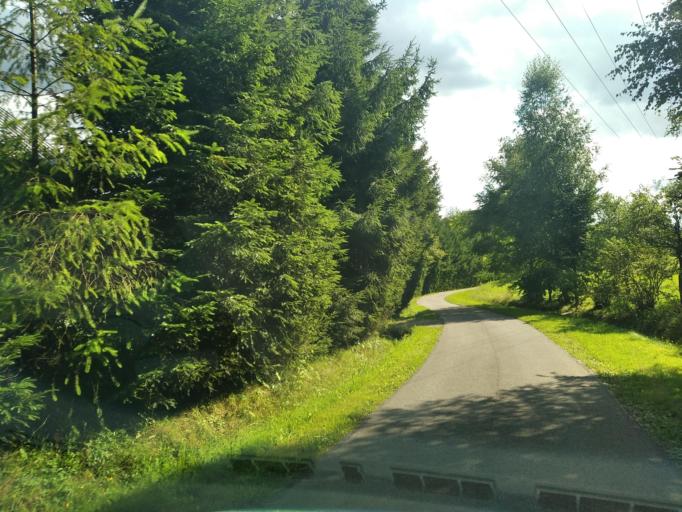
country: PL
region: Subcarpathian Voivodeship
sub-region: Powiat strzyzowski
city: Polomia
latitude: 49.9003
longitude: 21.9192
